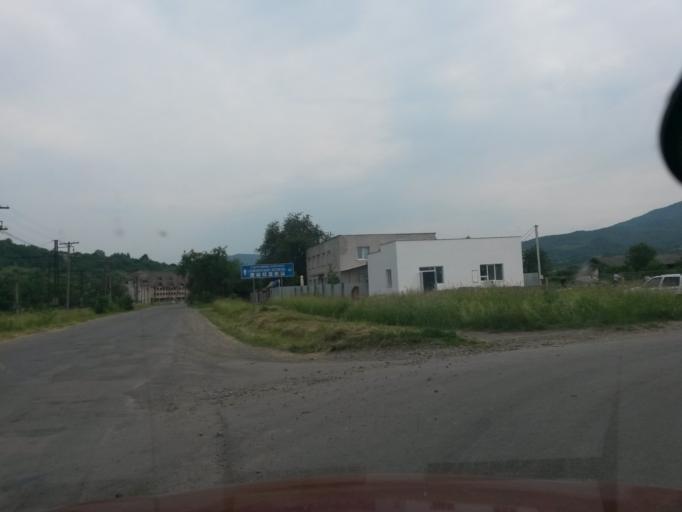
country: UA
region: Zakarpattia
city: Velykyi Bereznyi
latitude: 48.9055
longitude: 22.4585
